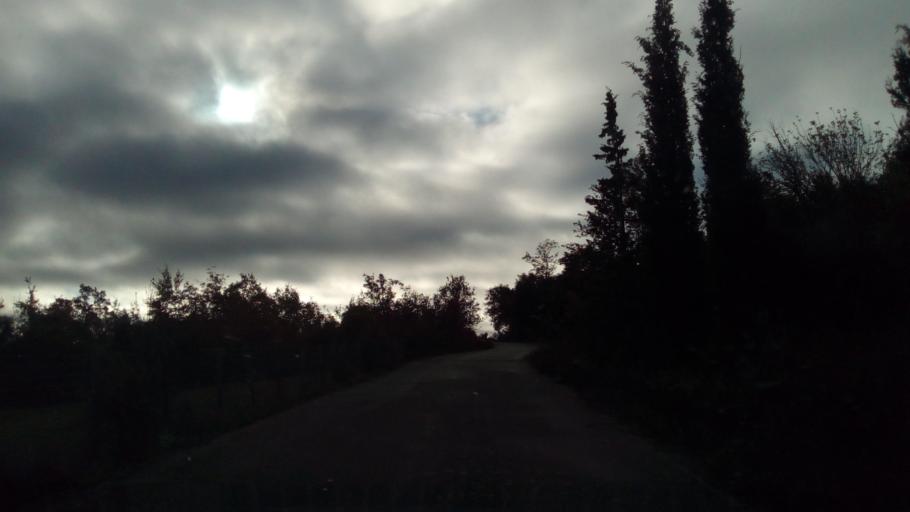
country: GR
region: West Greece
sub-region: Nomos Aitolias kai Akarnanias
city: Nafpaktos
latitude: 38.5232
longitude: 21.9783
